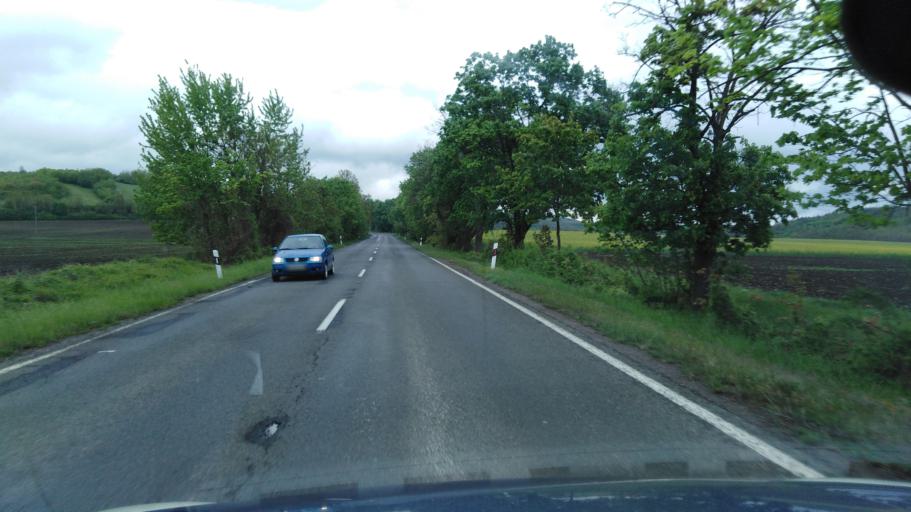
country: HU
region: Nograd
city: Szecseny
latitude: 48.1144
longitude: 19.5491
